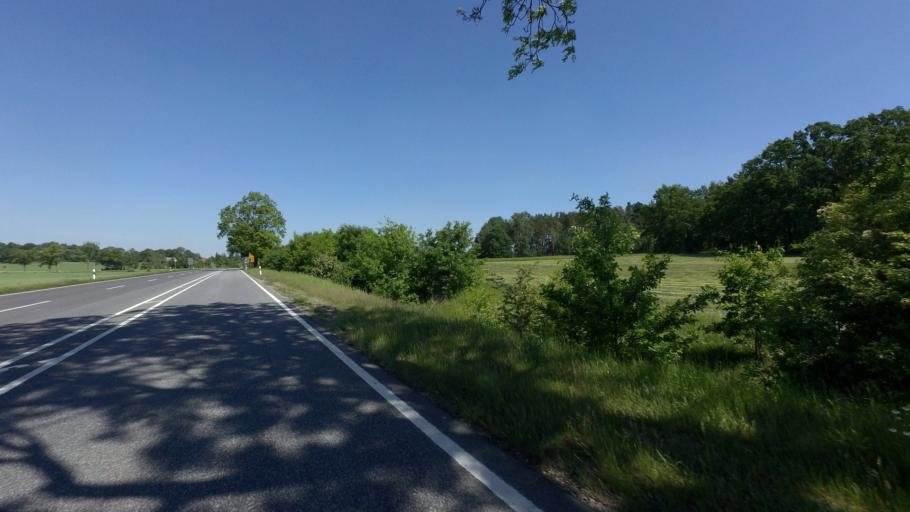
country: DE
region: Brandenburg
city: Cottbus
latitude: 51.6729
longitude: 14.3564
